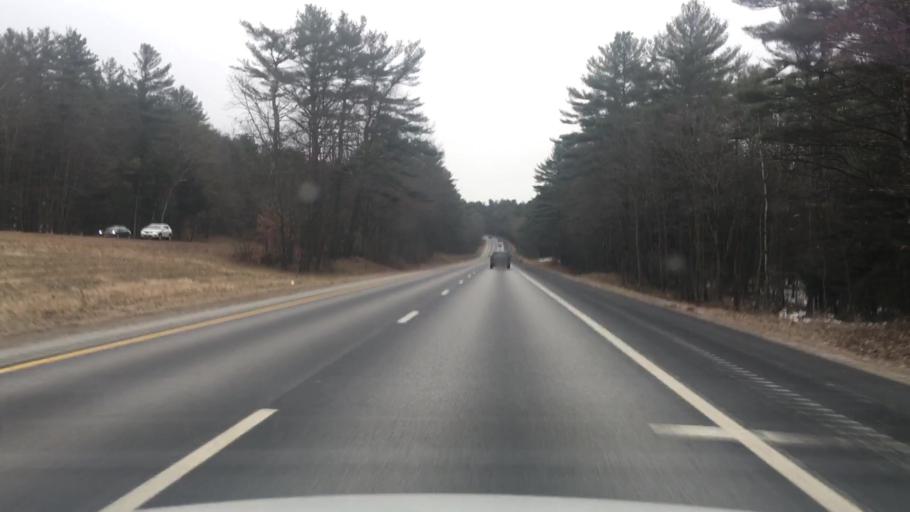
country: US
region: New Hampshire
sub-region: Merrimack County
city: Hopkinton
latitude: 43.1775
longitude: -71.6239
